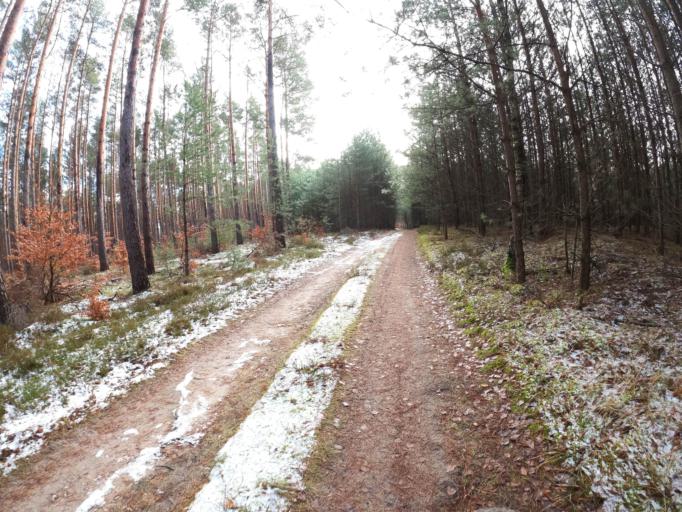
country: PL
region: Lubusz
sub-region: Powiat slubicki
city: Cybinka
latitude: 52.2500
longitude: 14.7972
